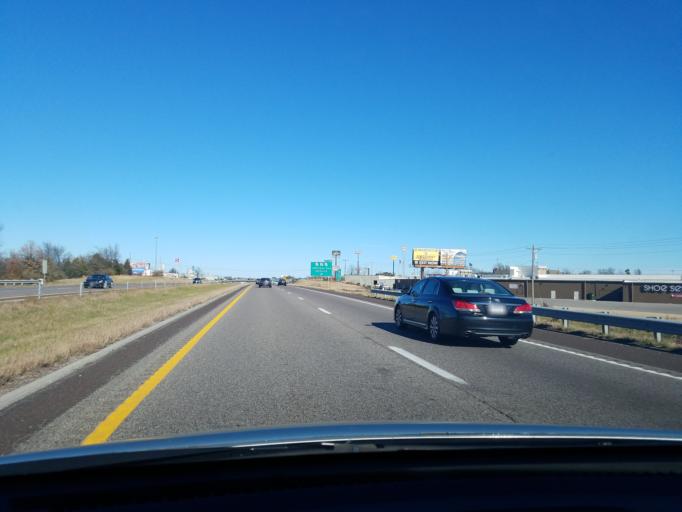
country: US
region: Missouri
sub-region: Laclede County
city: Lebanon
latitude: 37.6649
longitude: -92.6535
